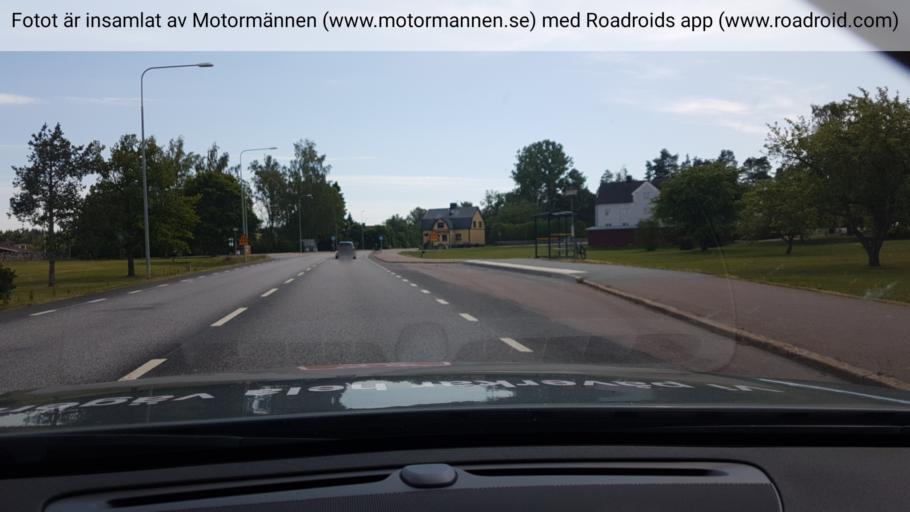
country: SE
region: Uppsala
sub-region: Osthammars Kommun
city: Gimo
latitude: 60.1734
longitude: 18.1930
